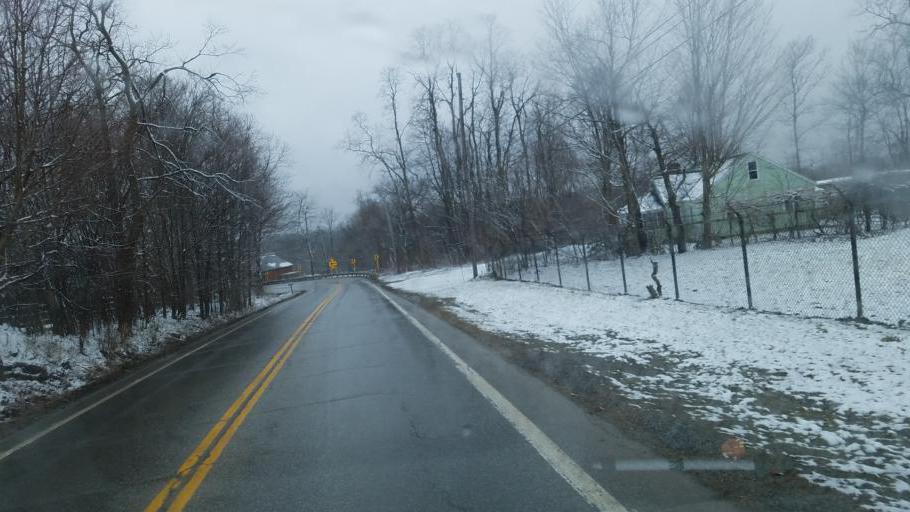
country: US
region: Ohio
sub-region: Geauga County
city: Middlefield
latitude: 41.3745
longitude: -81.0704
